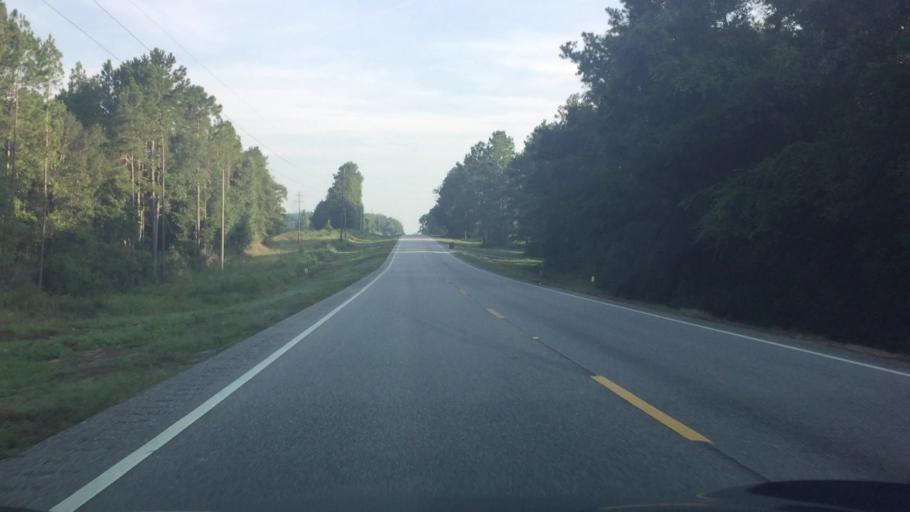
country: US
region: Alabama
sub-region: Covington County
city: Florala
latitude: 31.1265
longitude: -86.4555
